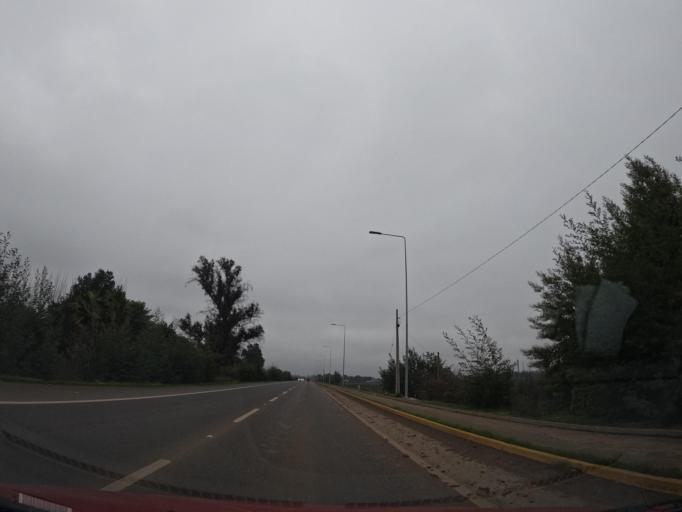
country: CL
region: Maule
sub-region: Provincia de Talca
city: San Clemente
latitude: -35.5243
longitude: -71.4846
